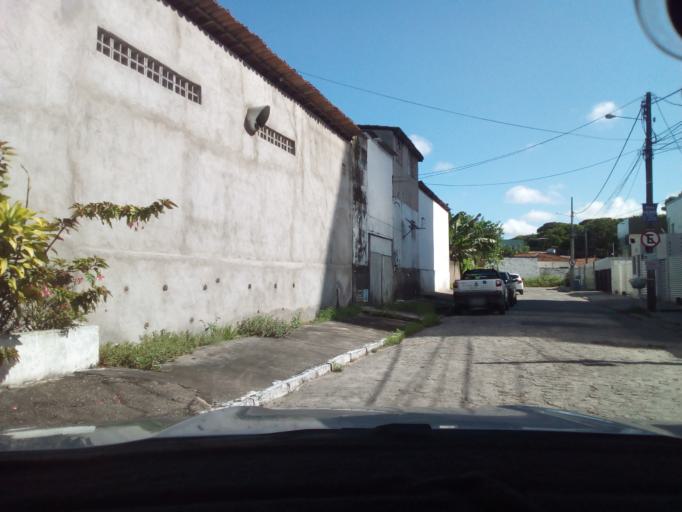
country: BR
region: Paraiba
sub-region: Joao Pessoa
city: Joao Pessoa
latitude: -7.1441
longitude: -34.8474
